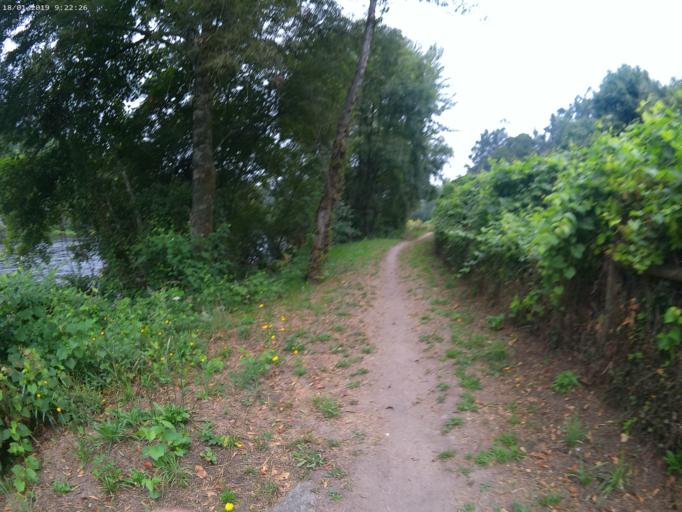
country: PT
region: Viana do Castelo
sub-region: Ponte da Barca
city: Ponte da Barca
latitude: 41.8033
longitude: -8.4619
